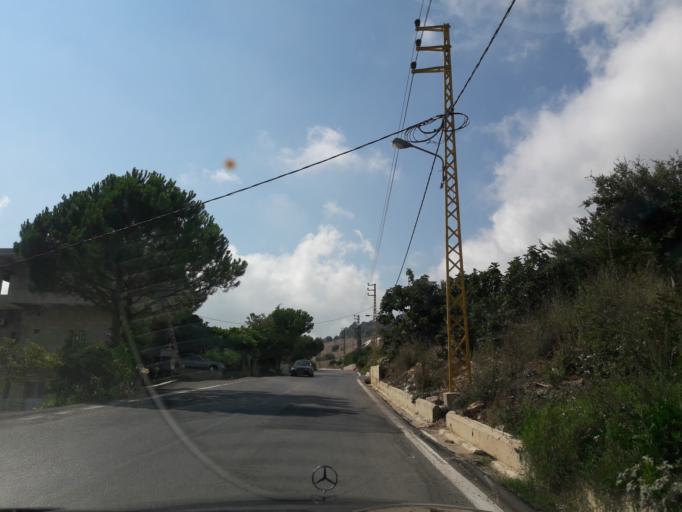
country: LB
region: Mont-Liban
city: Djounie
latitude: 33.9650
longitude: 35.7737
